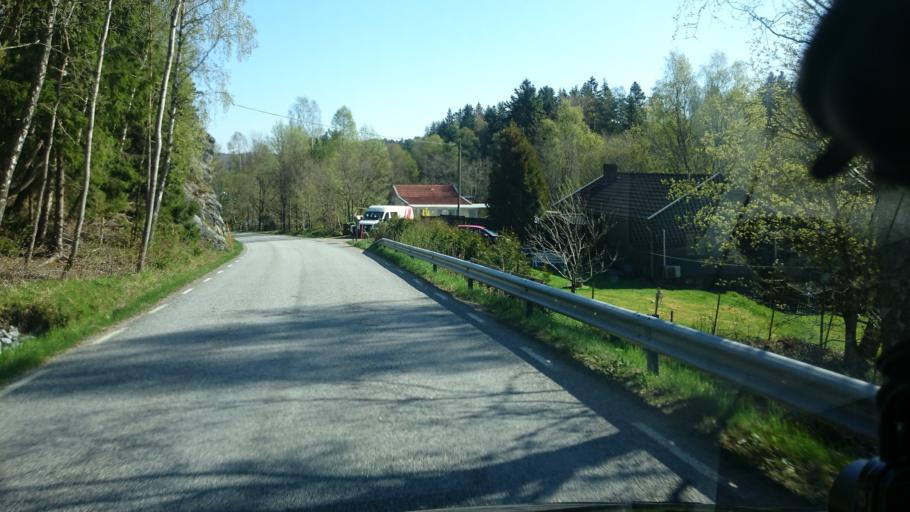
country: SE
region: Vaestra Goetaland
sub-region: Munkedals Kommun
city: Munkedal
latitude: 58.4220
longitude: 11.6921
